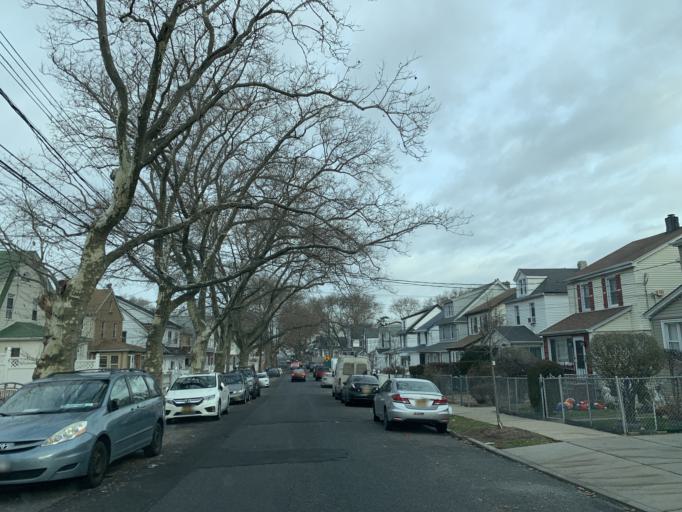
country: US
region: New York
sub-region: Queens County
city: Jamaica
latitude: 40.6866
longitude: -73.8101
